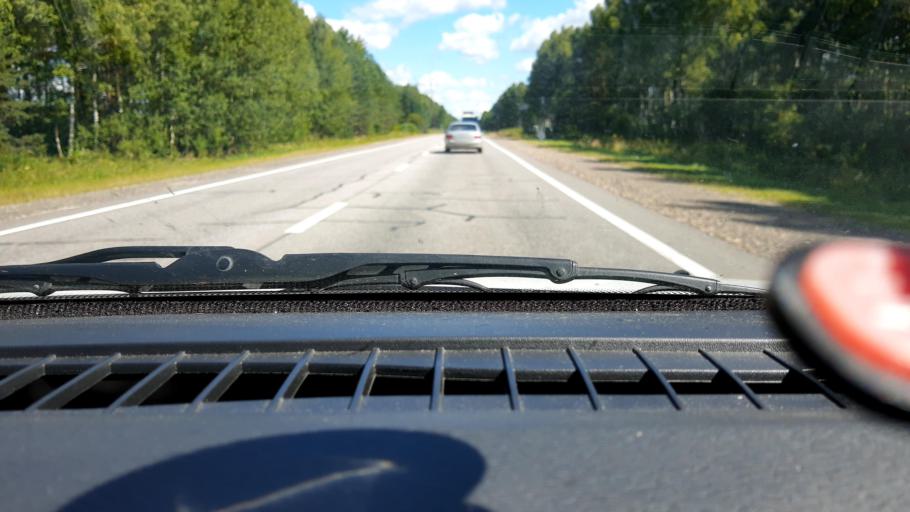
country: RU
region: Nizjnij Novgorod
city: Arzamas
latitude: 55.5544
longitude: 43.9460
